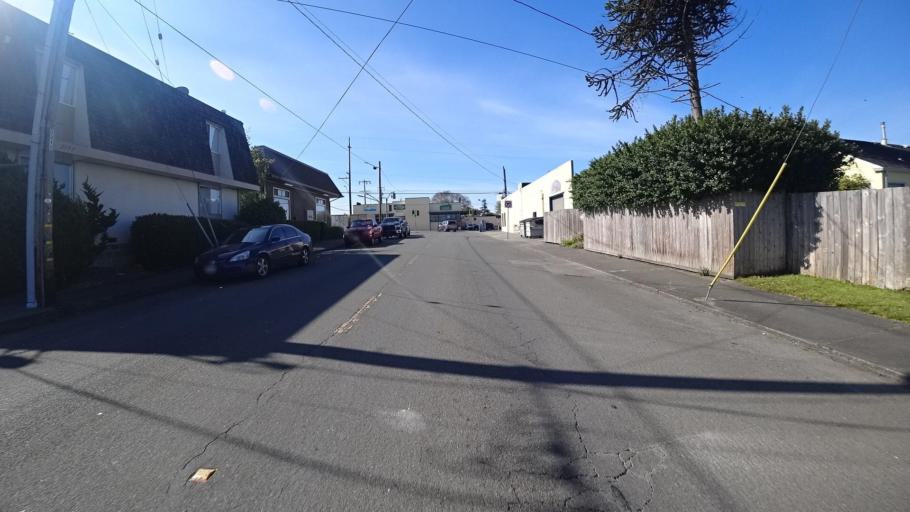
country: US
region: California
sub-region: Humboldt County
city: Bayview
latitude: 40.7811
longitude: -124.1752
